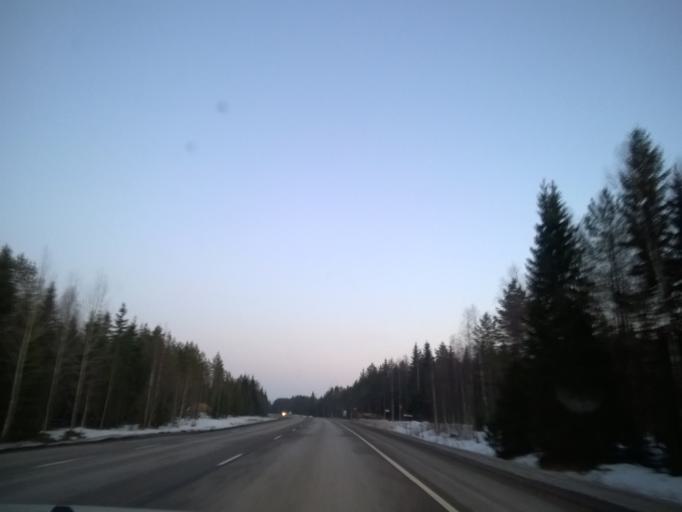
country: FI
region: Northern Ostrobothnia
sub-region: Nivala-Haapajaervi
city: Pyhaesalmi
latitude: 63.7934
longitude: 25.9186
